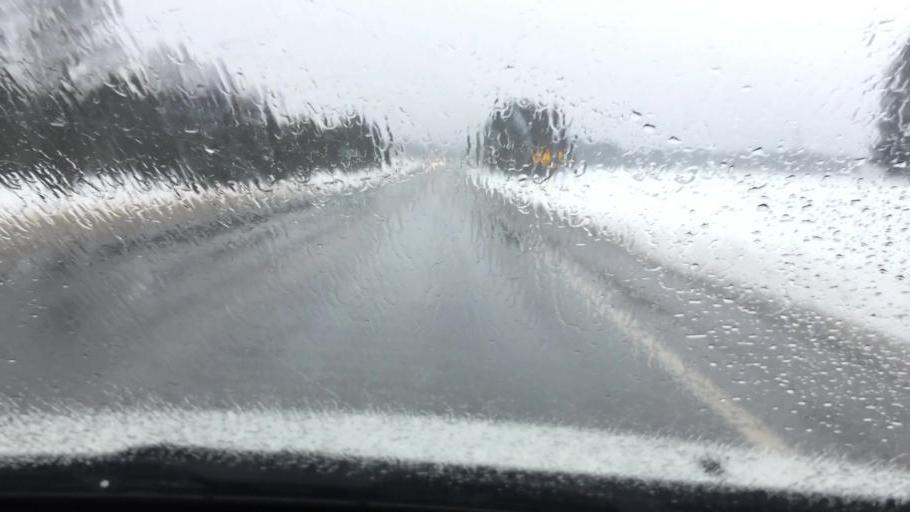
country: US
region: Michigan
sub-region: Antrim County
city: Mancelona
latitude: 44.9165
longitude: -85.0510
